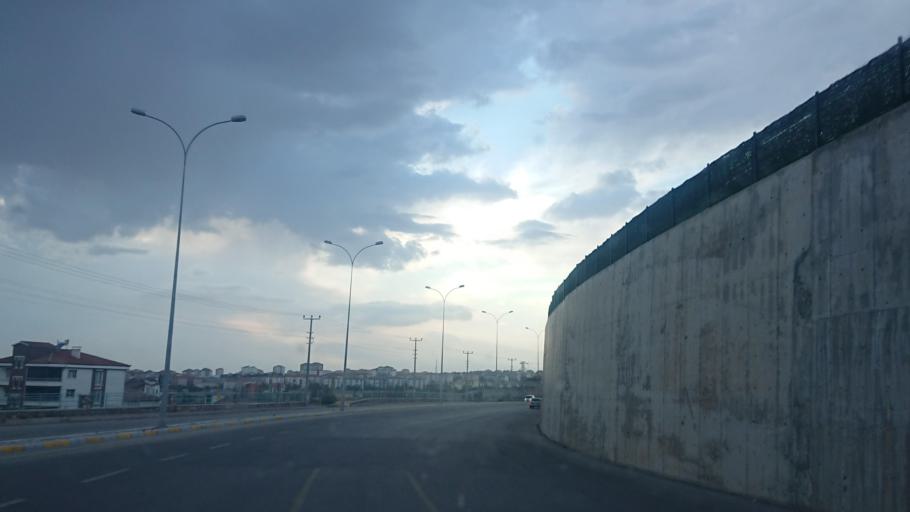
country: TR
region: Aksaray
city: Aksaray
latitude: 38.4037
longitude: 34.0142
